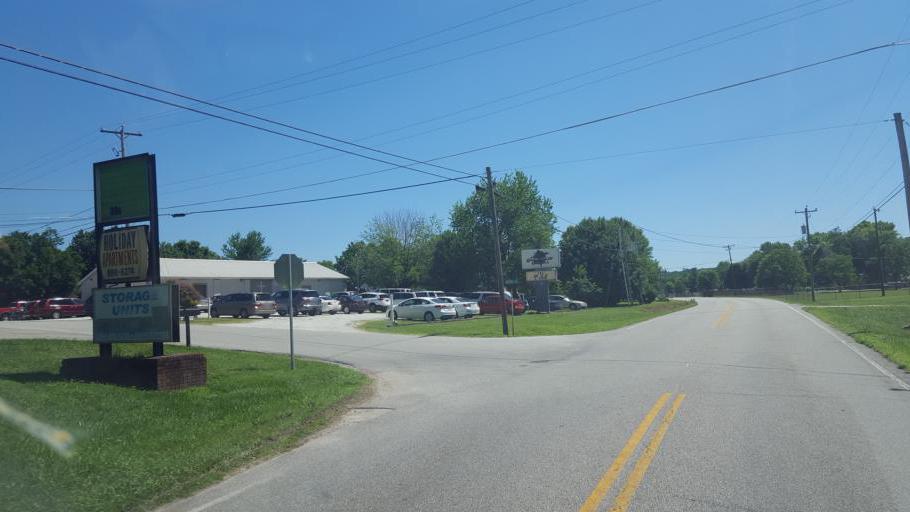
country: US
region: West Virginia
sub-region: Cabell County
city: Pea Ridge
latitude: 38.4430
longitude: -82.3409
